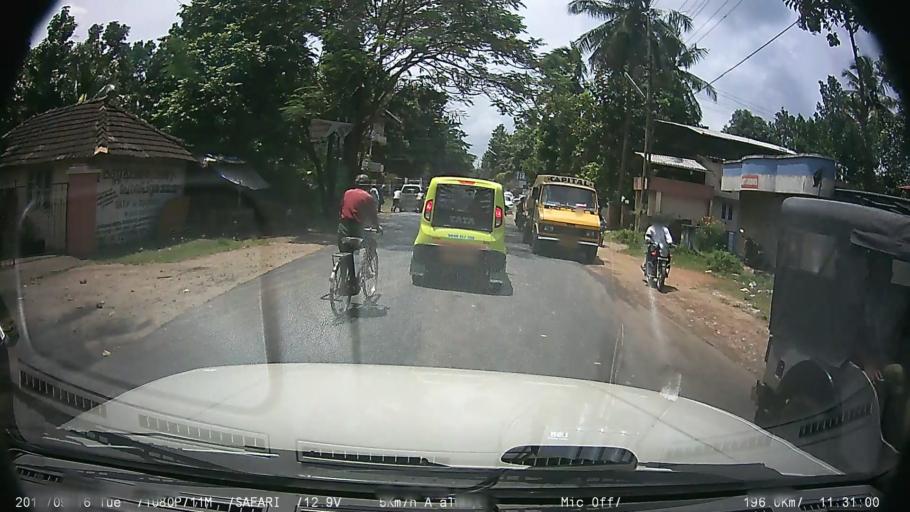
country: IN
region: Kerala
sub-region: Kottayam
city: Changanacheri
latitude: 9.4760
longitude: 76.5282
